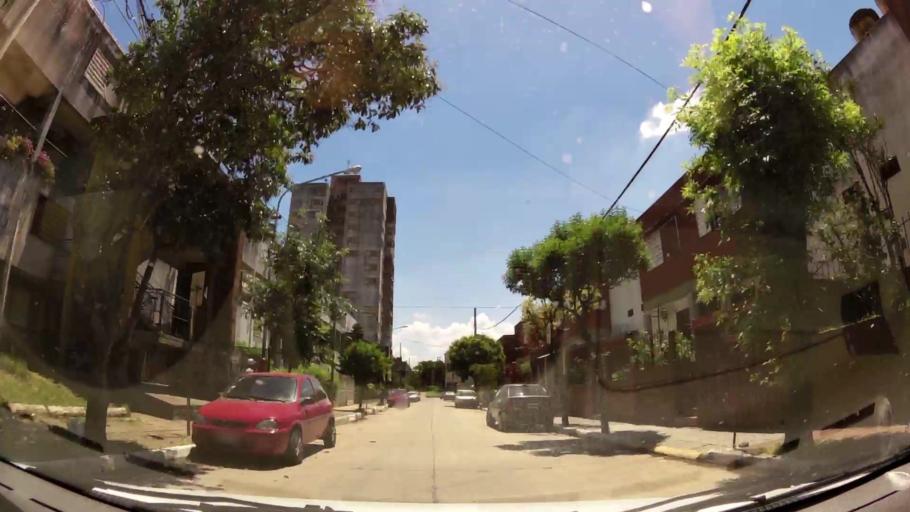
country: AR
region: Buenos Aires
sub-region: Partido de Merlo
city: Merlo
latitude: -34.6540
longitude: -58.7091
